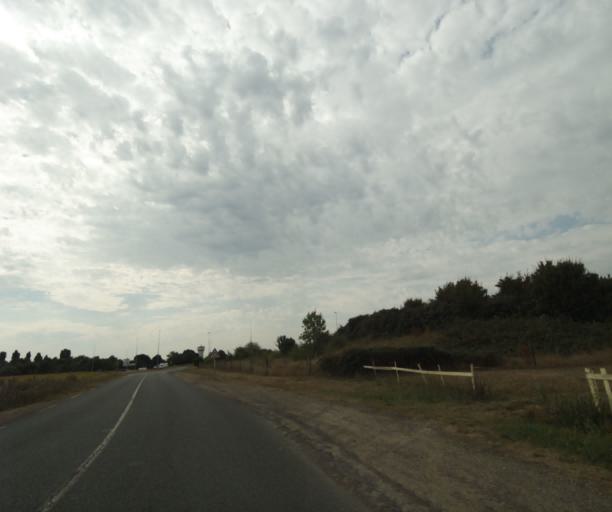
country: FR
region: Poitou-Charentes
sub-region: Departement de la Charente-Maritime
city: Tonnay-Charente
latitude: 45.9553
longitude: -0.8788
